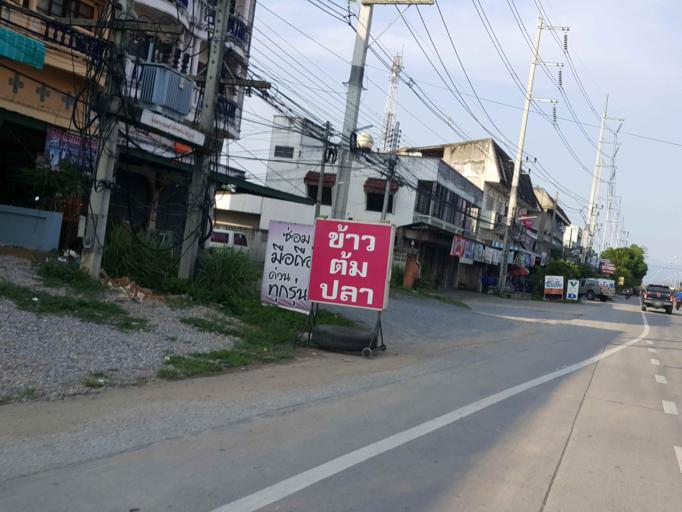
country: TH
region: Chiang Mai
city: San Sai
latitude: 18.8479
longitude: 99.0812
